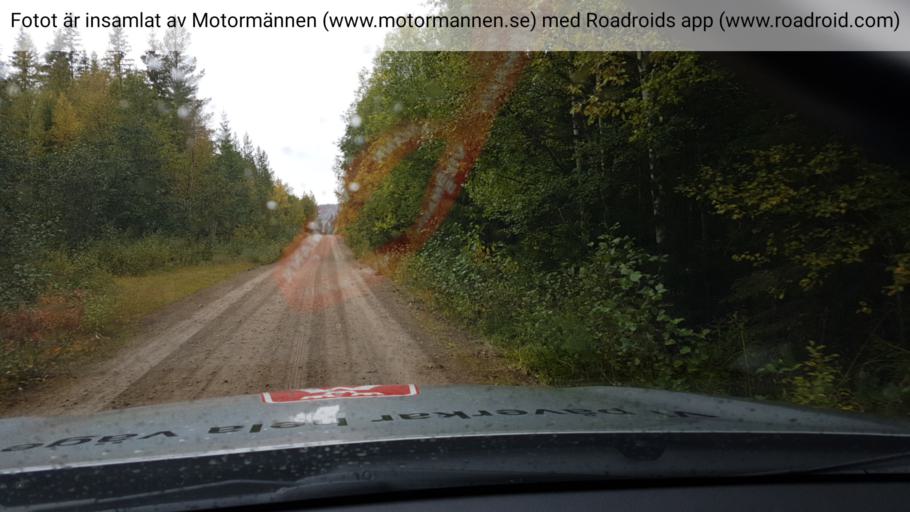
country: SE
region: Jaemtland
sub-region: Harjedalens Kommun
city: Sveg
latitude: 62.2441
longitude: 13.3088
